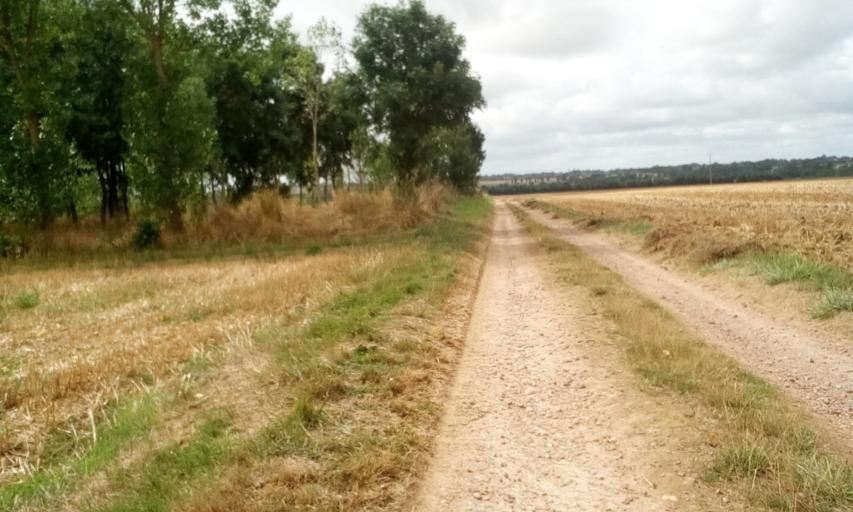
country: FR
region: Lower Normandy
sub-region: Departement du Calvados
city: Tilly-sur-Seulles
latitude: 49.2032
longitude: -0.6130
